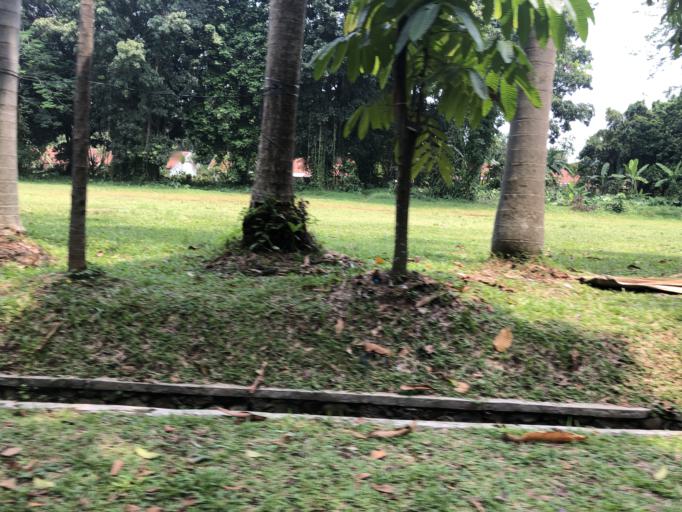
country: ID
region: West Java
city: Ciampea
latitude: -6.5538
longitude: 106.7229
